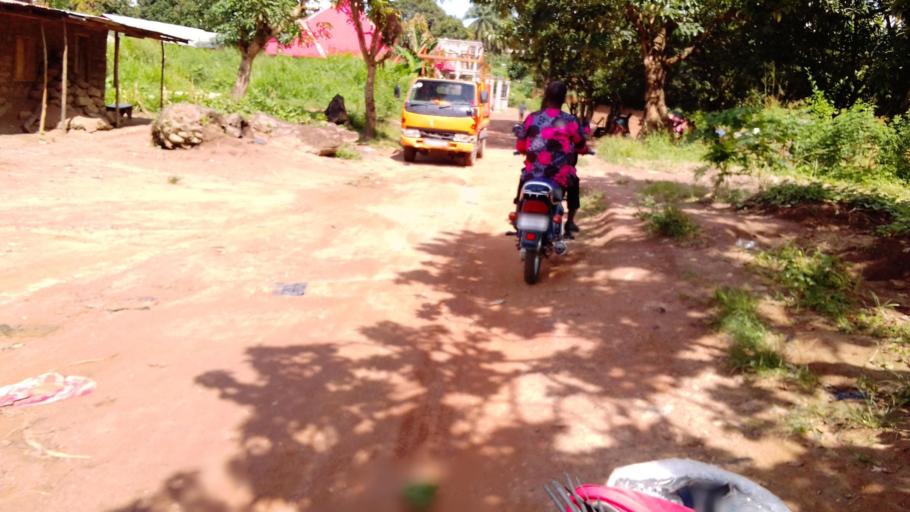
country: SL
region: Eastern Province
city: Koidu
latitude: 8.6618
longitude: -10.9770
